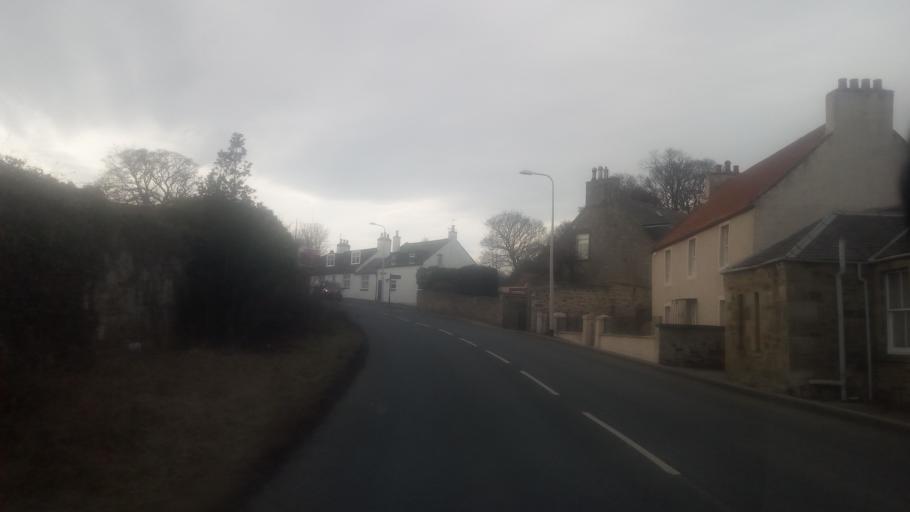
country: GB
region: Scotland
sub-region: East Lothian
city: Tranent
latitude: 55.9501
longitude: -2.9560
